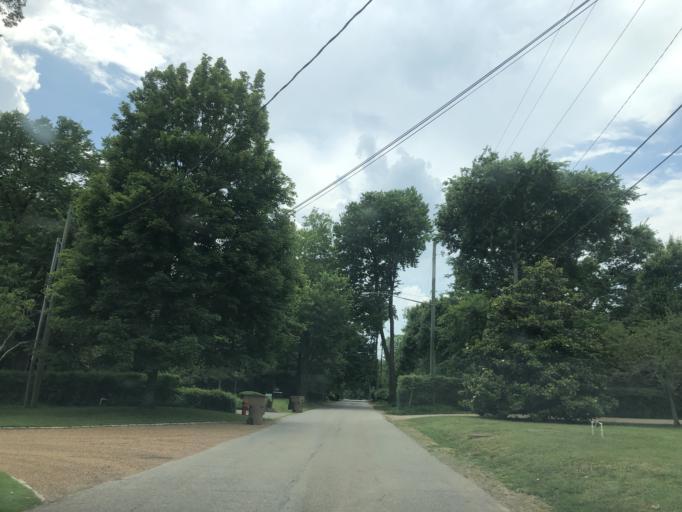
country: US
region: Tennessee
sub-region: Davidson County
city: Belle Meade
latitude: 36.1190
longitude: -86.8200
